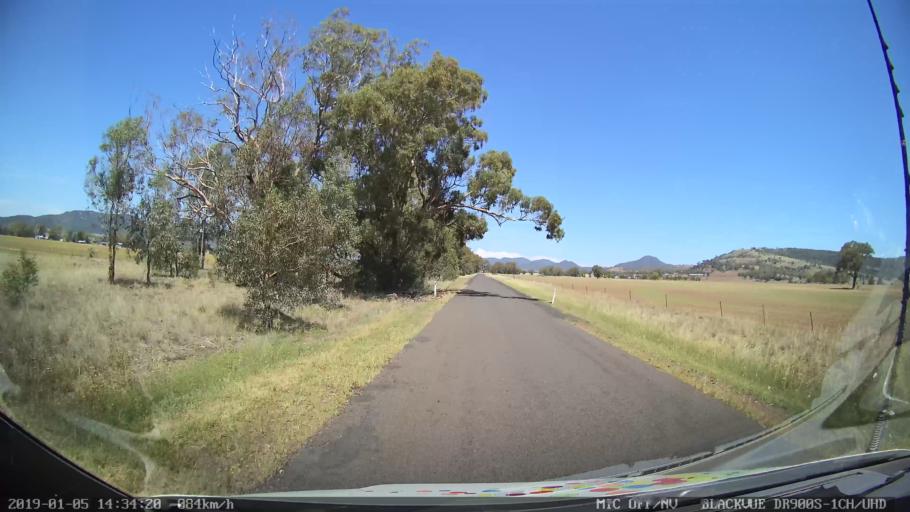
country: AU
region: New South Wales
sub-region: Tamworth Municipality
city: Phillip
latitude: -31.2320
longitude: 150.6403
